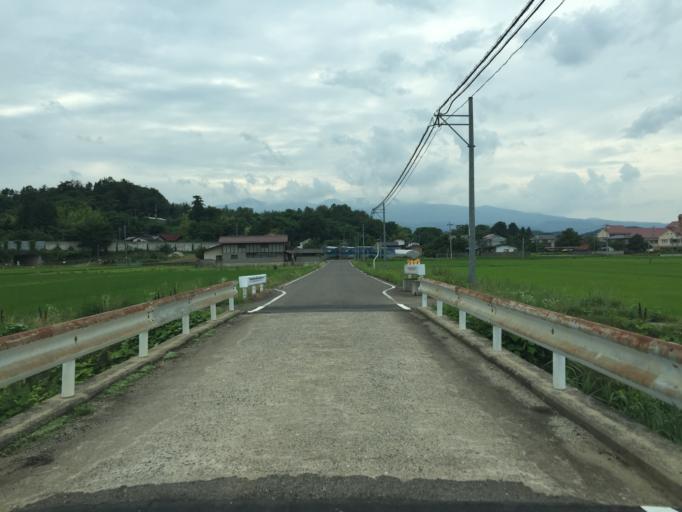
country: JP
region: Fukushima
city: Fukushima-shi
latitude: 37.7119
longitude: 140.4503
